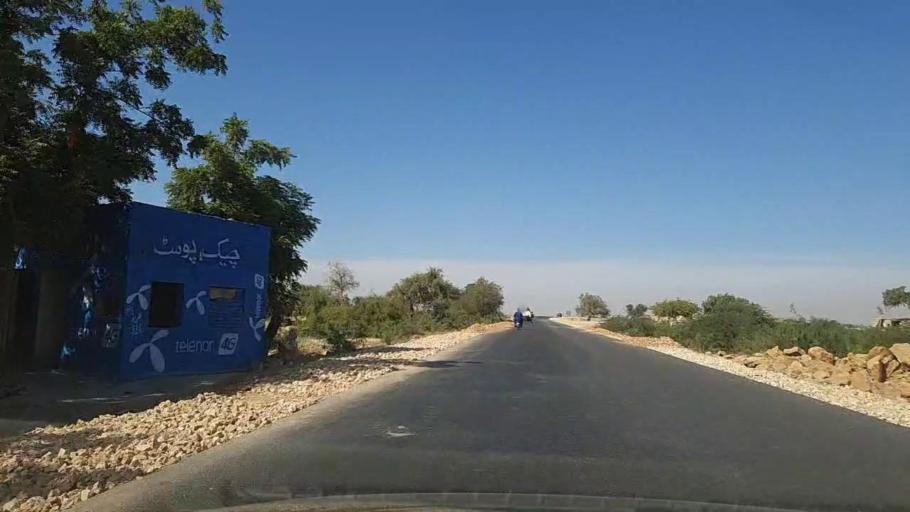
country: PK
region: Sindh
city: Kotri
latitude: 25.2930
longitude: 68.2050
